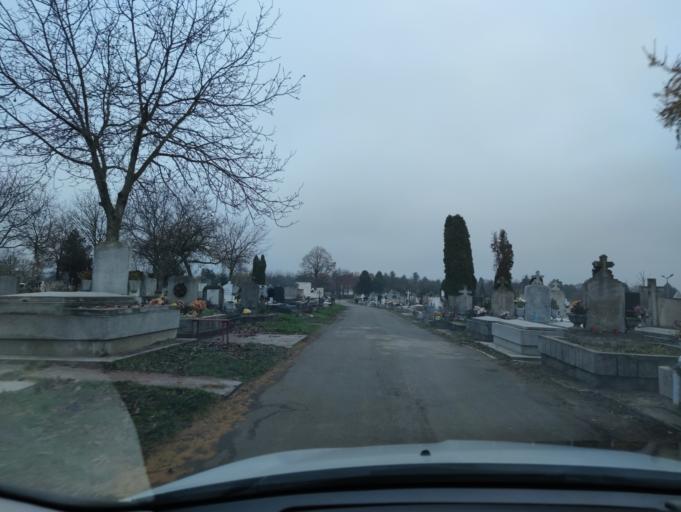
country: RO
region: Bihor
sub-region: Comuna Biharea
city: Oradea
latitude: 47.0389
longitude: 21.9264
